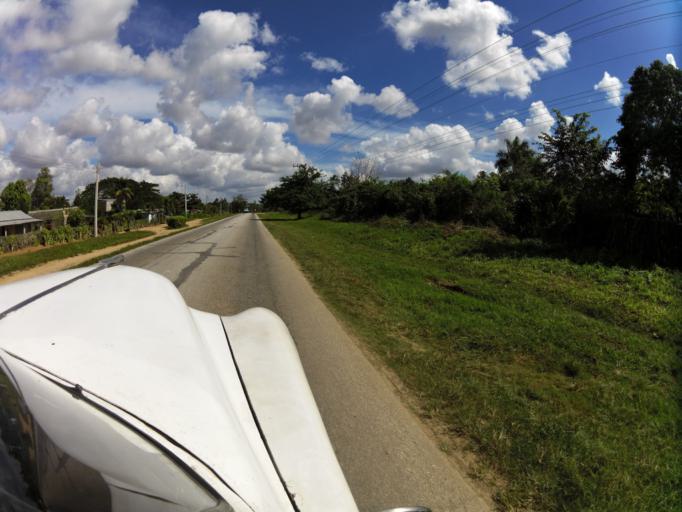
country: CU
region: Holguin
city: Cacocum
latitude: 20.8622
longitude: -76.4441
